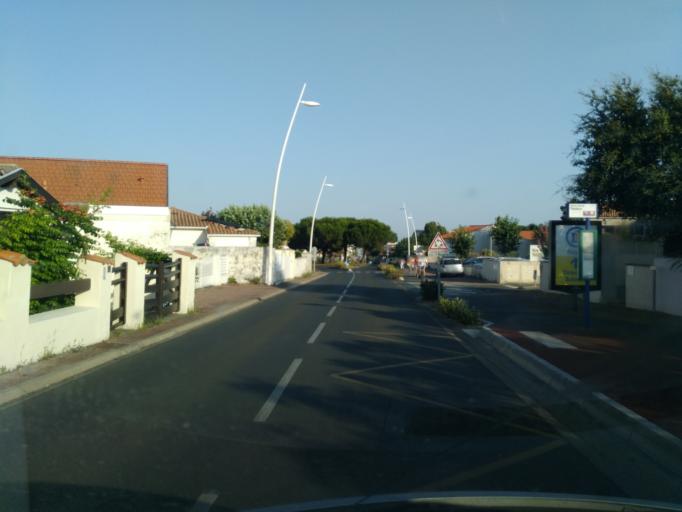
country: FR
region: Poitou-Charentes
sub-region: Departement de la Charente-Maritime
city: Vaux-sur-Mer
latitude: 45.6316
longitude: -1.0567
